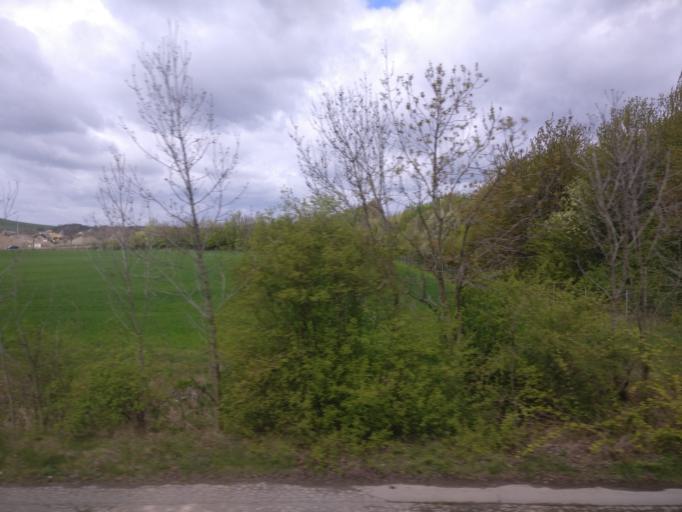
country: DE
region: Lower Saxony
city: Vienenburg
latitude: 51.9242
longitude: 10.5098
